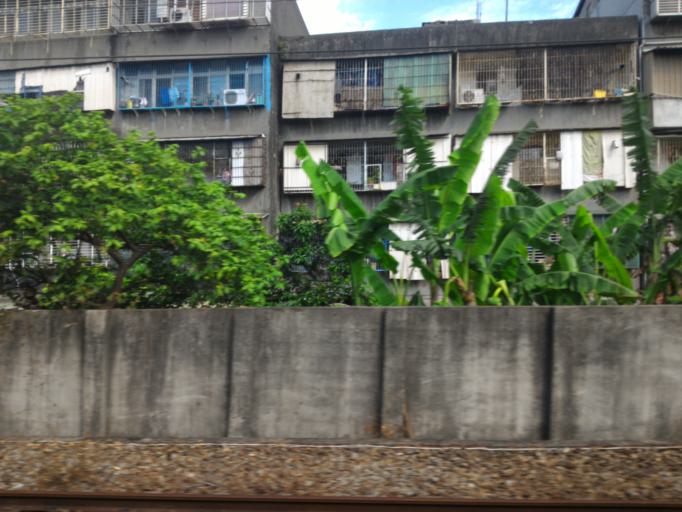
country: TW
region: Taipei
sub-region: Taipei
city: Banqiao
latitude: 24.9948
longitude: 121.4262
